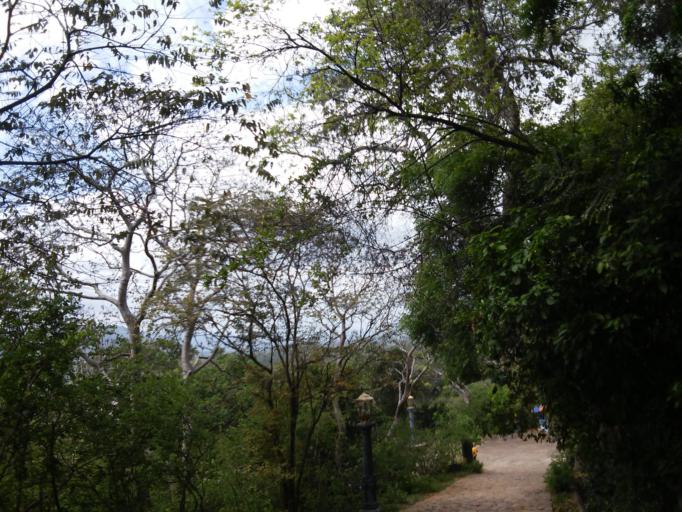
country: LK
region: Central
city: Dambulla
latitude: 7.8552
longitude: 80.6498
